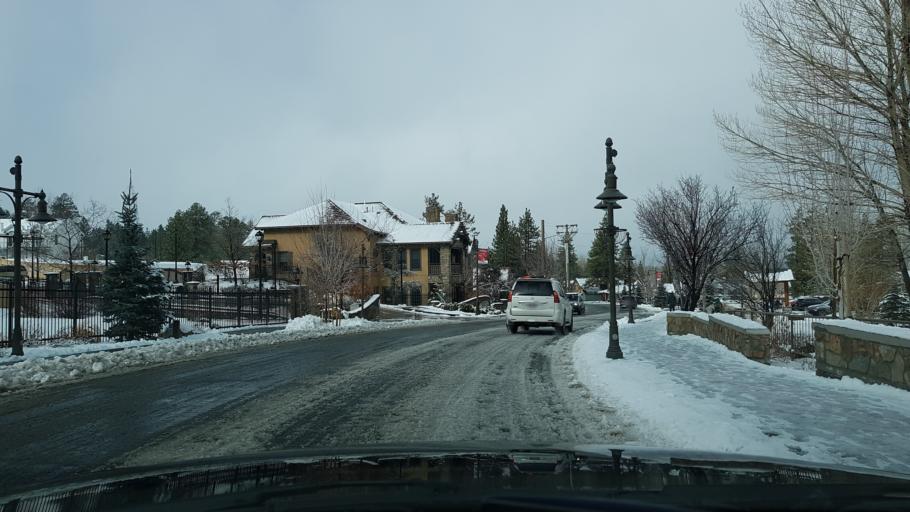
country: US
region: California
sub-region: San Bernardino County
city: Big Bear Lake
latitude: 34.2401
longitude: -116.9144
